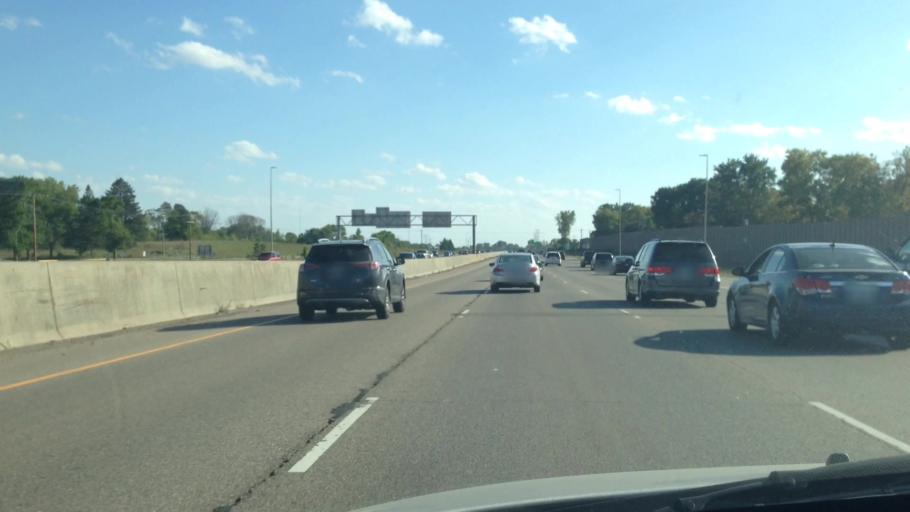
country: US
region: Minnesota
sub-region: Ramsey County
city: Mounds View
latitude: 45.1052
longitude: -93.1888
